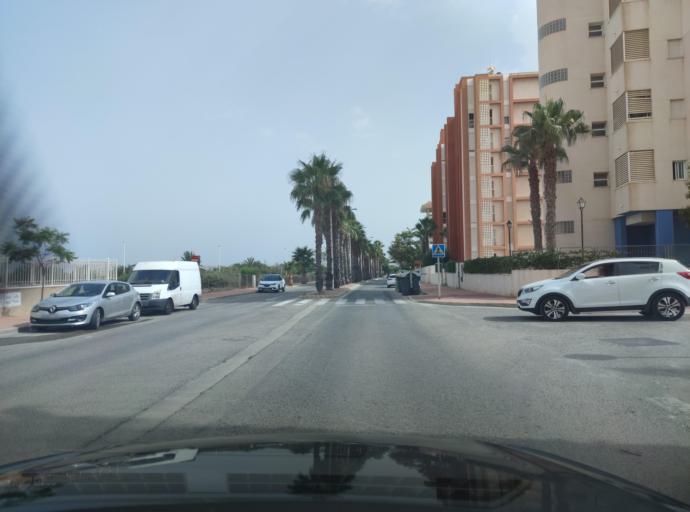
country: ES
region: Valencia
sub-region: Provincia de Alicante
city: Guardamar del Segura
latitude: 38.1013
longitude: -0.6557
